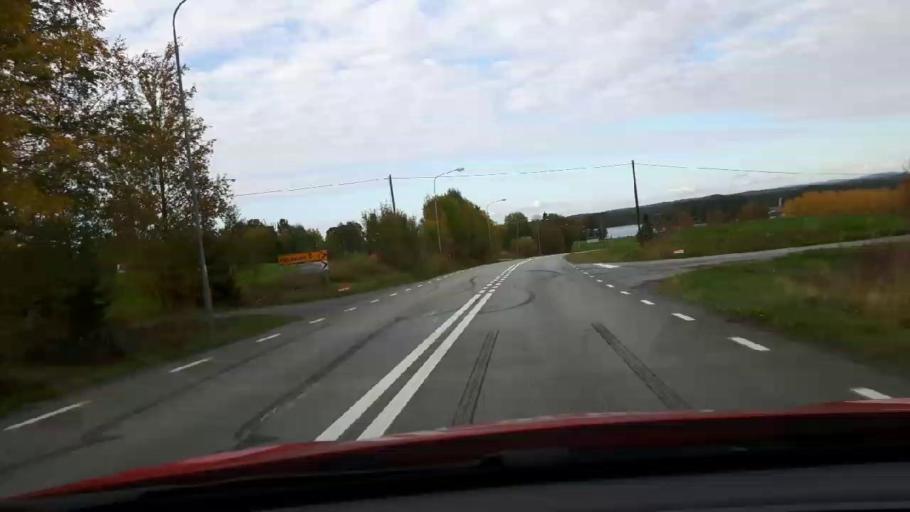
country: SE
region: Jaemtland
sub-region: Krokoms Kommun
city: Valla
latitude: 63.2406
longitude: 14.0016
